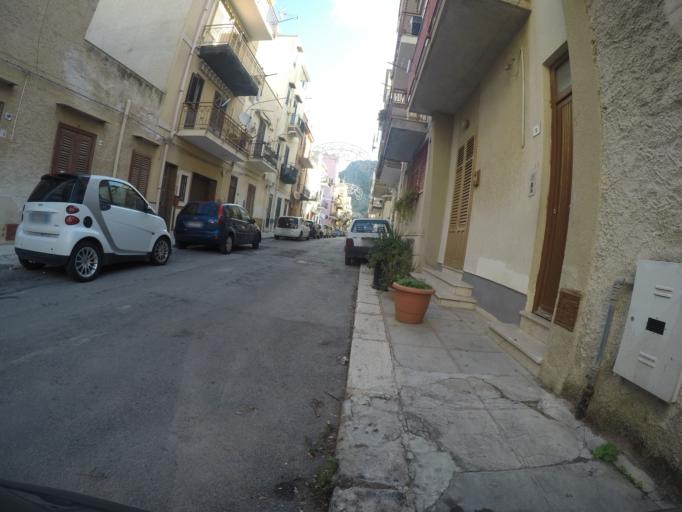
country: IT
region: Sicily
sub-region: Palermo
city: Isola delle Femmine
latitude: 38.2002
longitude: 13.2777
